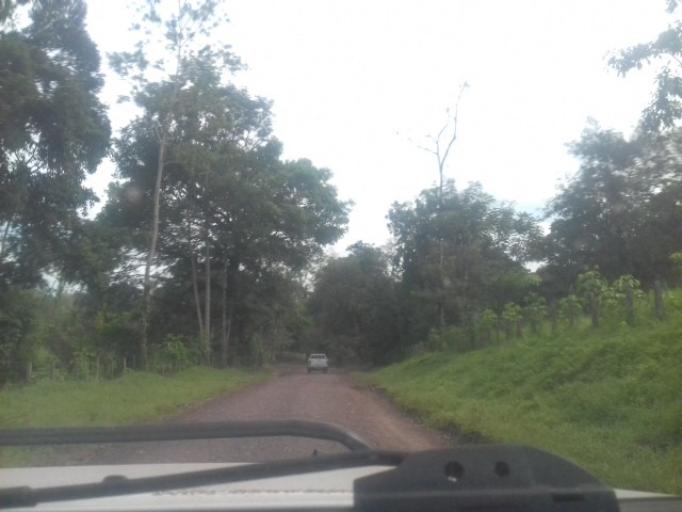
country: NI
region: Atlantico Norte (RAAN)
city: Waslala
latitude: 13.4227
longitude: -85.3154
